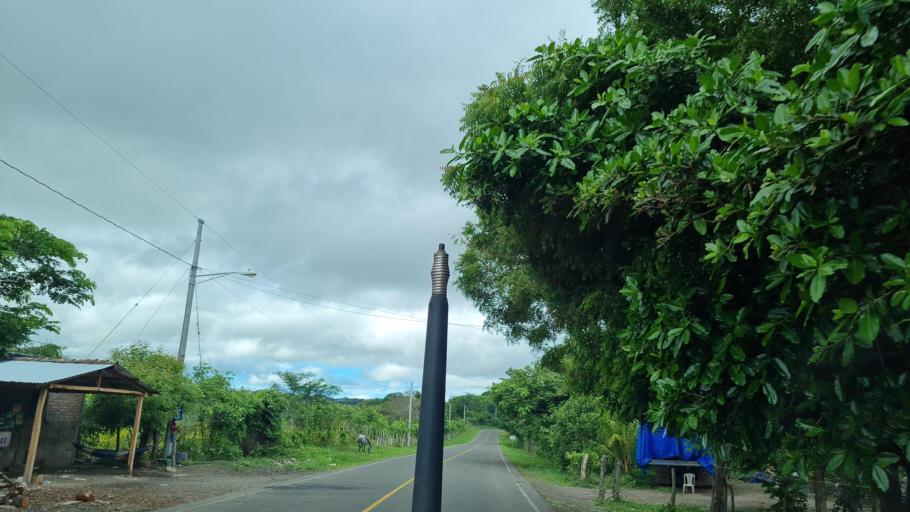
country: NI
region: Boaco
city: San Jose de los Remates
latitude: 12.5983
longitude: -85.8985
